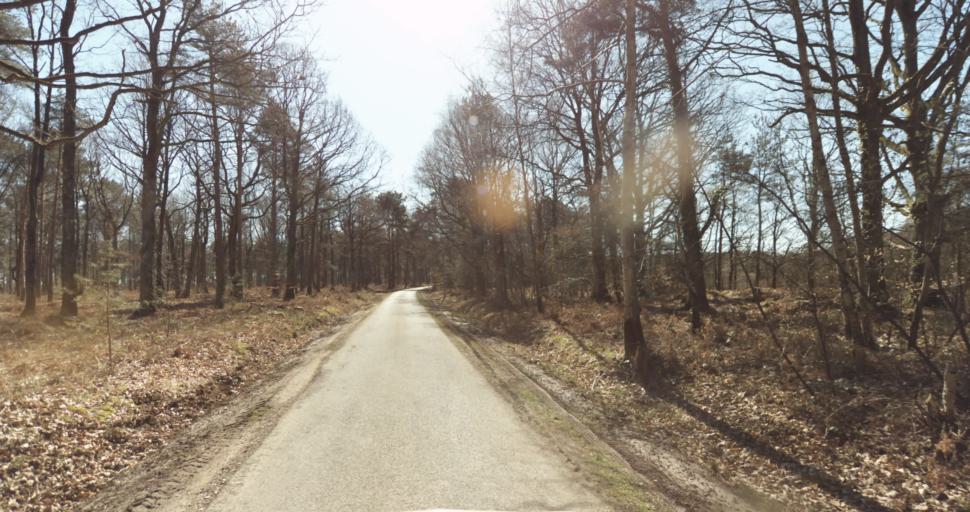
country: FR
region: Lower Normandy
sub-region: Departement du Calvados
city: Livarot
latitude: 48.9716
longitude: 0.0957
